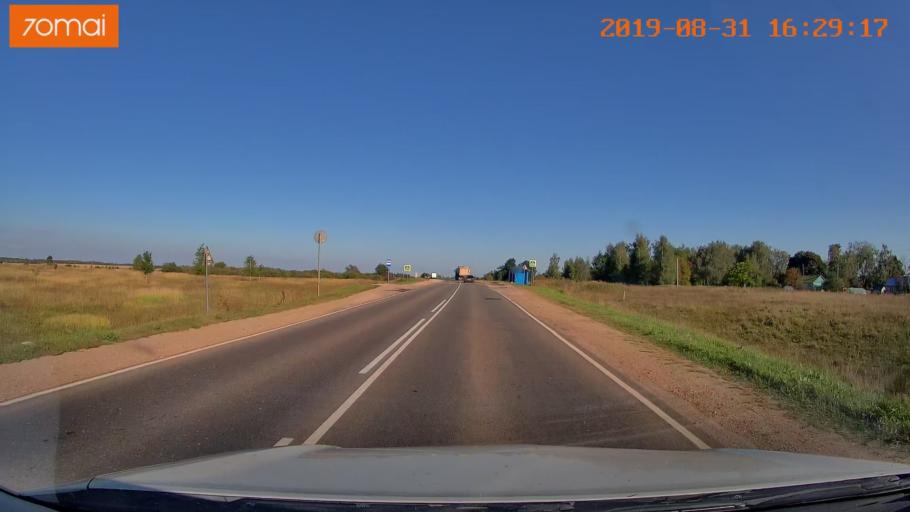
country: RU
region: Kaluga
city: Babynino
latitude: 54.5062
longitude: 35.8010
